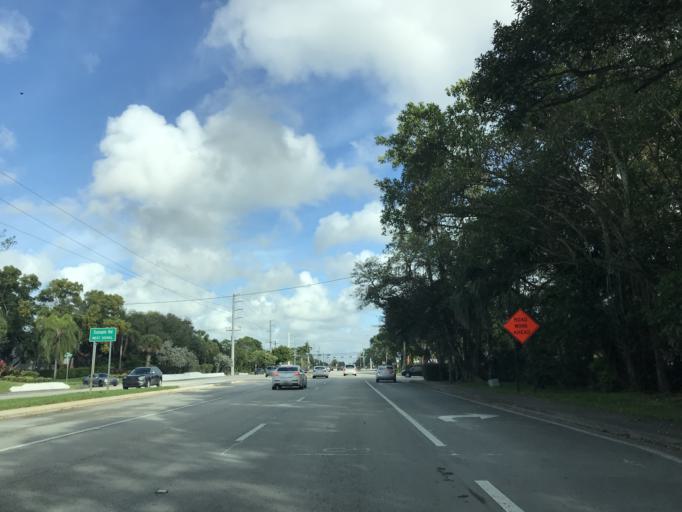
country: US
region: Florida
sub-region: Broward County
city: Coconut Creek
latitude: 26.2714
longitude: -80.1863
